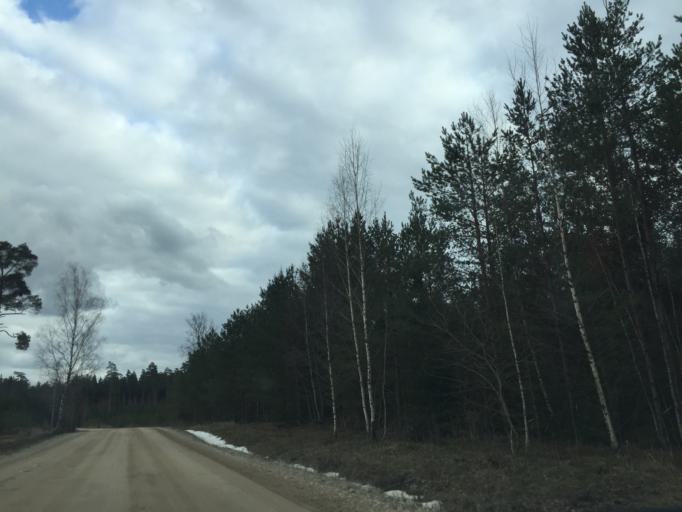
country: LV
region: Ogre
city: Jumprava
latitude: 56.5879
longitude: 24.9940
